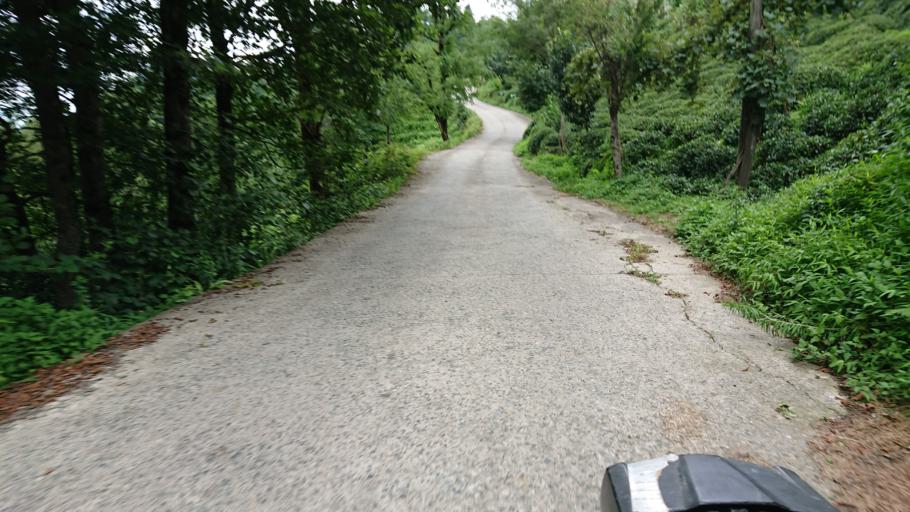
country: TR
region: Rize
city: Rize
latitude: 40.9752
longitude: 40.5170
